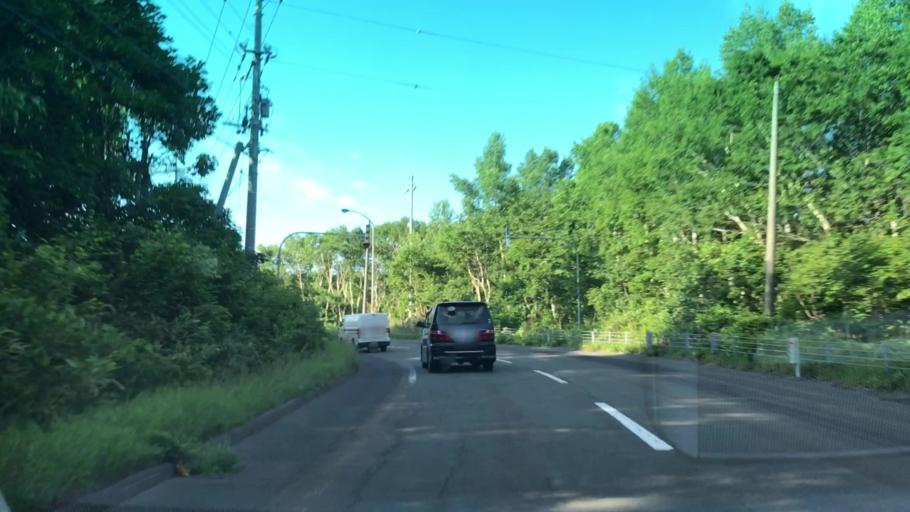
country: JP
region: Hokkaido
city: Otaru
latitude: 43.1283
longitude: 141.0130
